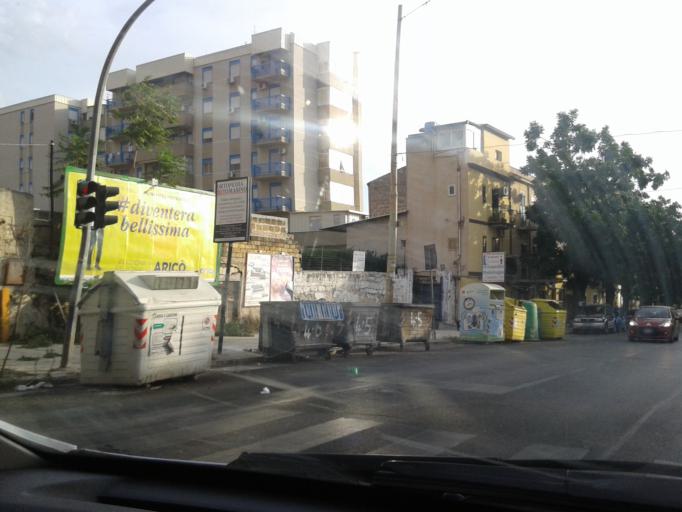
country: IT
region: Sicily
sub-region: Palermo
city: Monreale
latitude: 38.0947
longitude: 13.3099
